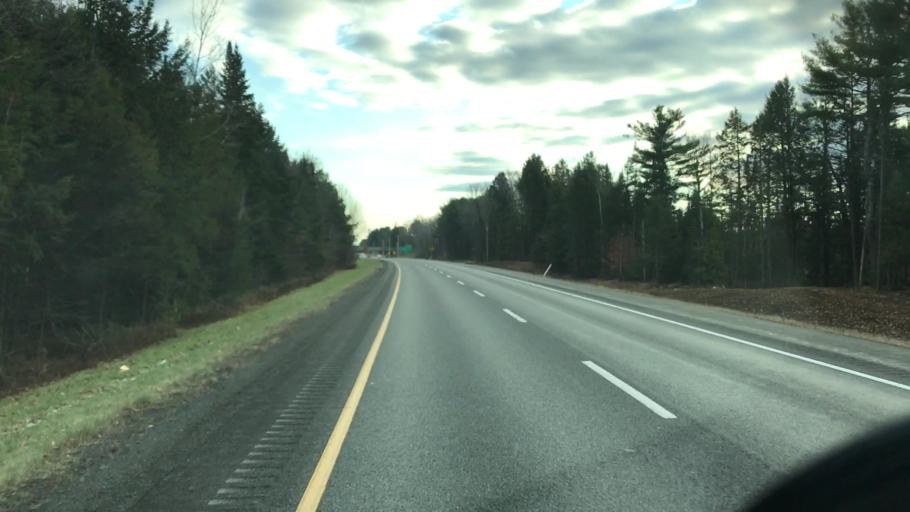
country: US
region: Maine
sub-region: Kennebec County
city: Oakland
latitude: 44.5131
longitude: -69.7029
